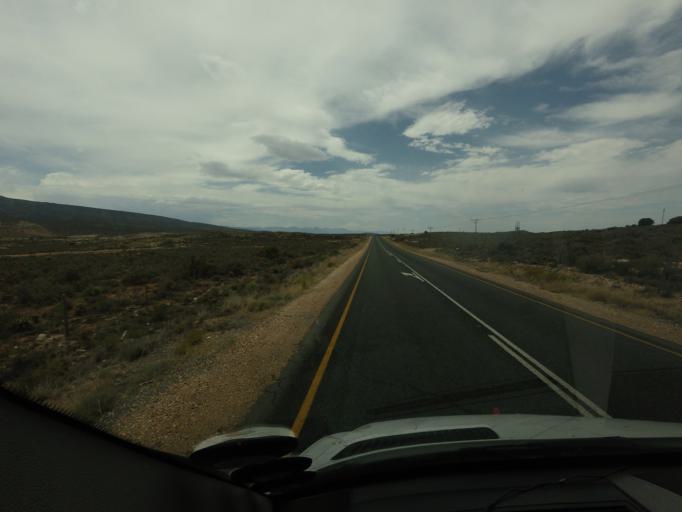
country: ZA
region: Western Cape
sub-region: Overberg District Municipality
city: Swellendam
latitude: -33.8452
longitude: 20.8626
